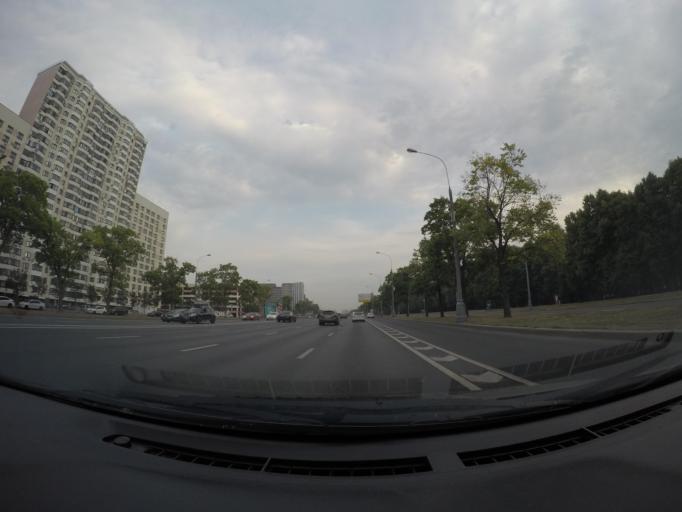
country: RU
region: Moscow
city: Orekhovo-Borisovo
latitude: 55.6053
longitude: 37.7201
